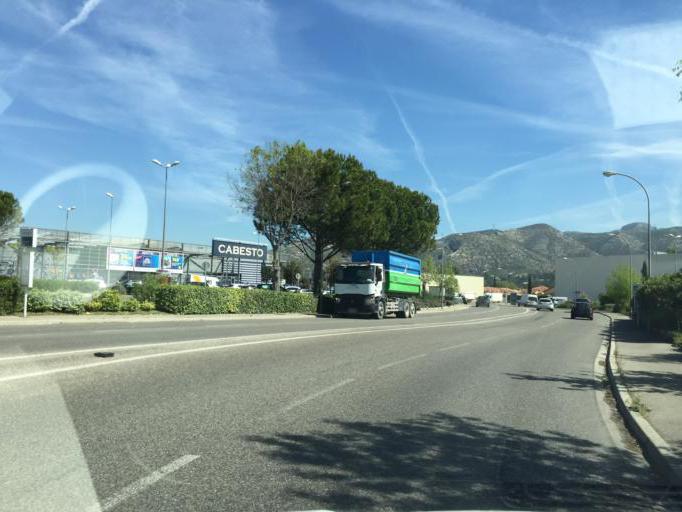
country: FR
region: Provence-Alpes-Cote d'Azur
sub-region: Departement des Bouches-du-Rhone
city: Aubagne
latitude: 43.2962
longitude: 5.5955
